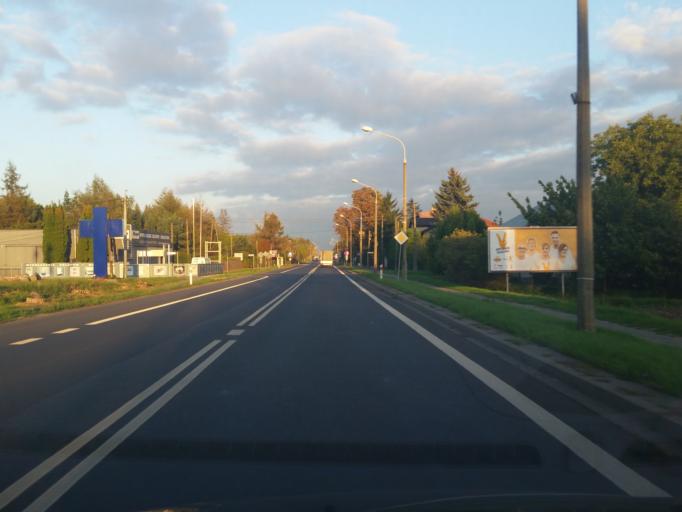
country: PL
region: Masovian Voivodeship
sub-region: Powiat warszawski zachodni
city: Ozarow Mazowiecki
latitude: 52.2106
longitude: 20.7871
